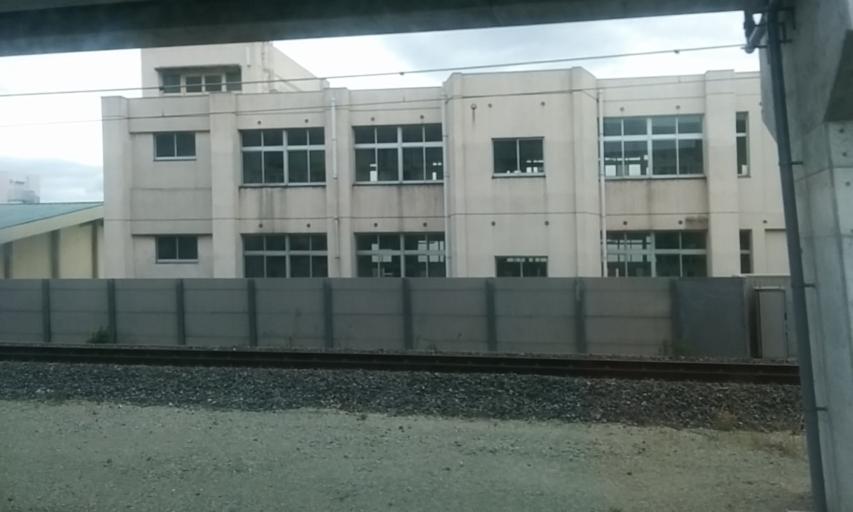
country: JP
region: Osaka
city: Moriguchi
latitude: 34.6918
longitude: 135.5481
